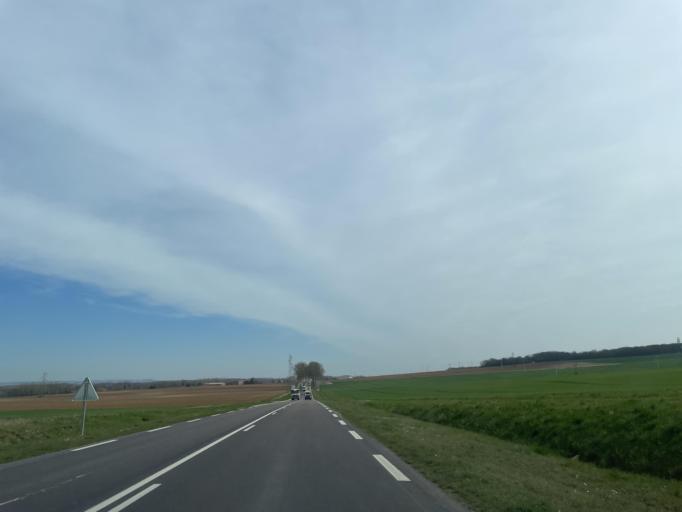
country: FR
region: Champagne-Ardenne
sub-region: Departement de l'Aube
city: Nogent-sur-Seine
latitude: 48.4995
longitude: 3.5493
